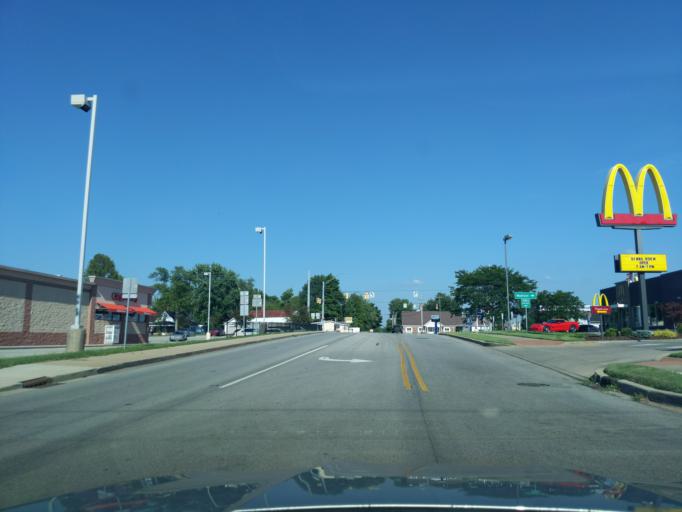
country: US
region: Indiana
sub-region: Ripley County
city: Versailles
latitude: 39.0699
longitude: -85.2552
